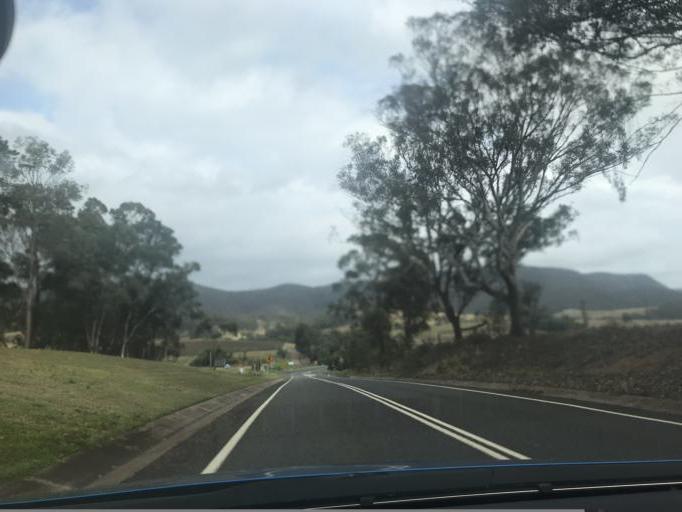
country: AU
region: New South Wales
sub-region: Cessnock
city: Cessnock
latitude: -32.8081
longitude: 151.2840
